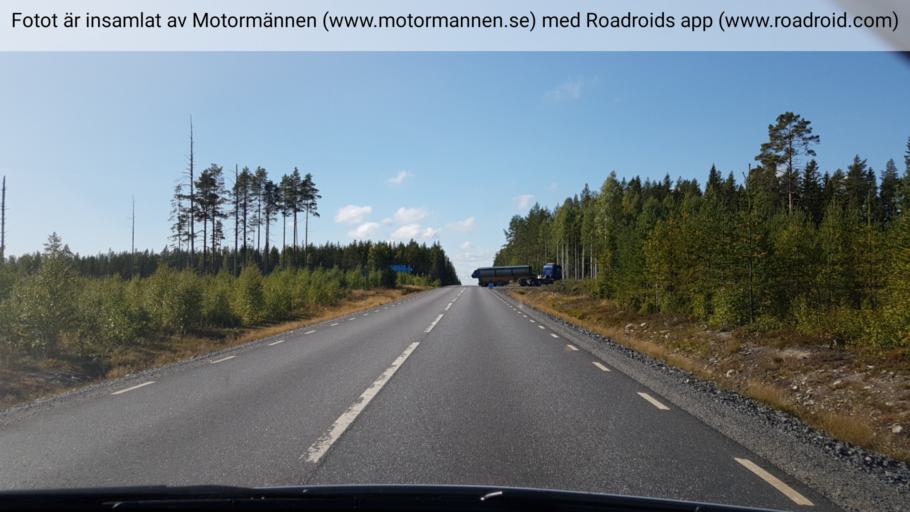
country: SE
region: Vaesterbotten
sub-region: Robertsfors Kommun
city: Robertsfors
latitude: 64.2070
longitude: 20.8710
